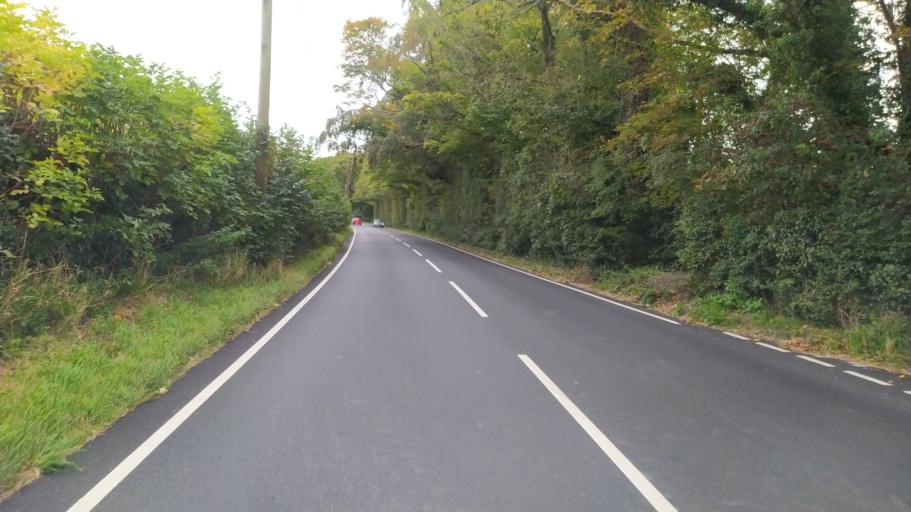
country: GB
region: England
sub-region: Dorset
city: Gillingham
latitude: 51.0430
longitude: -2.3066
